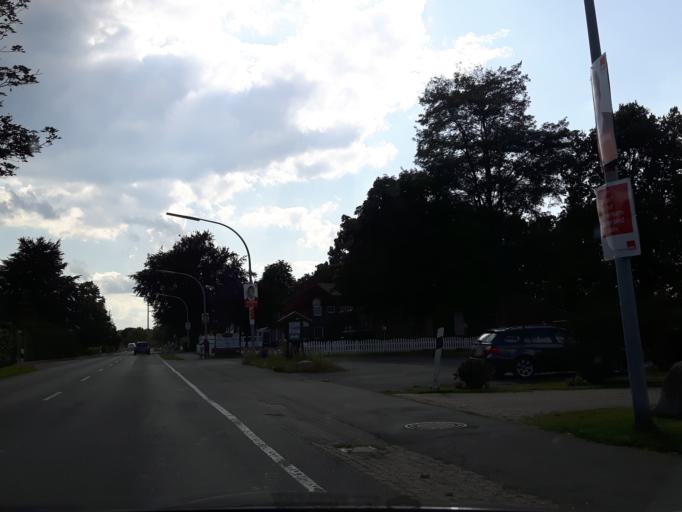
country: DE
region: Lower Saxony
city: Hatten
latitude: 53.0594
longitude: 8.3522
